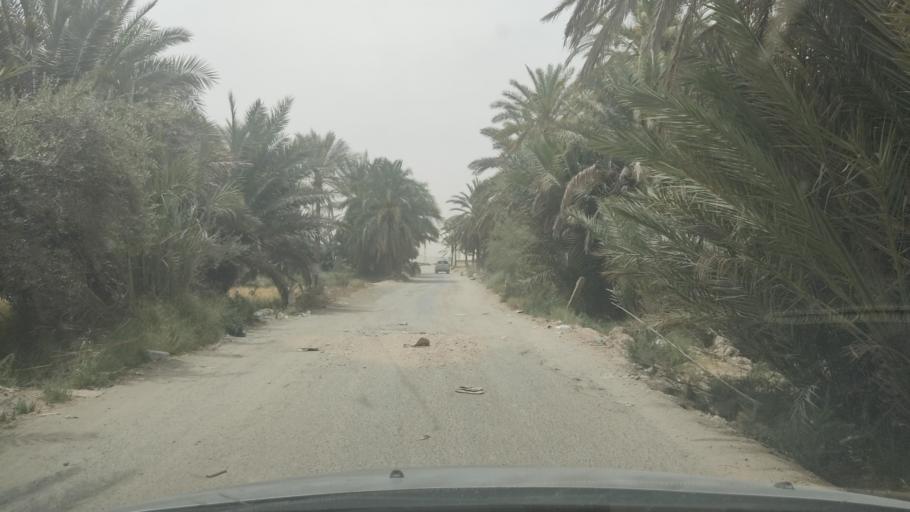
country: TN
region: Gafsa
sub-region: Gafsa Municipality
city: Gafsa
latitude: 34.3274
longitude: 8.9519
